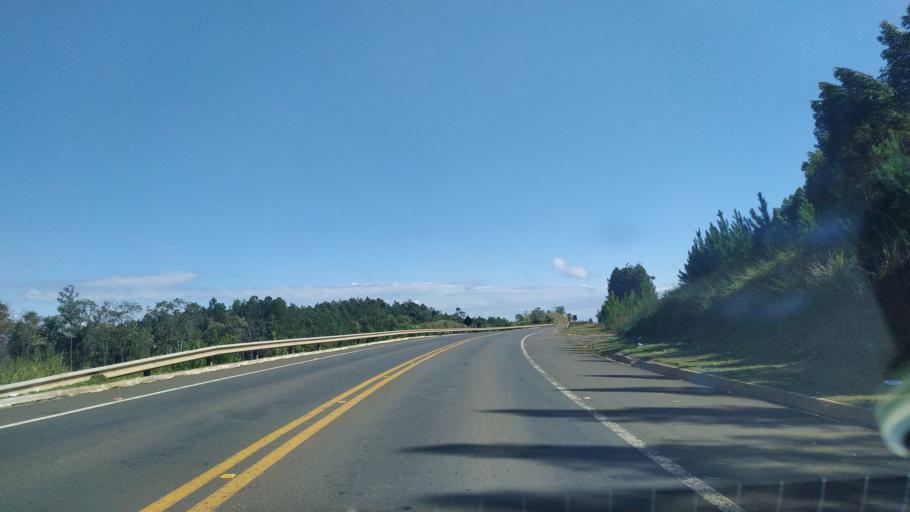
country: BR
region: Parana
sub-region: Ortigueira
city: Ortigueira
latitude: -24.2562
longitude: -50.7796
